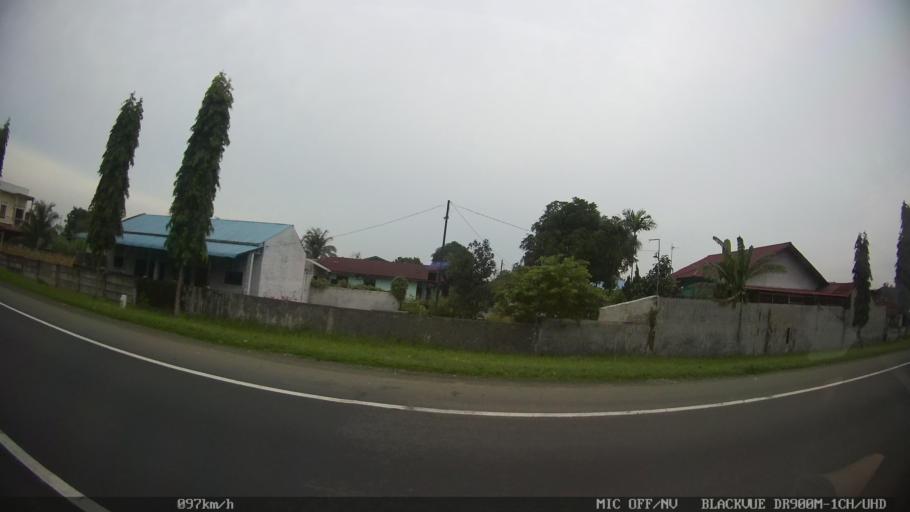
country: ID
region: North Sumatra
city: Medan
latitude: 3.5687
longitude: 98.7259
